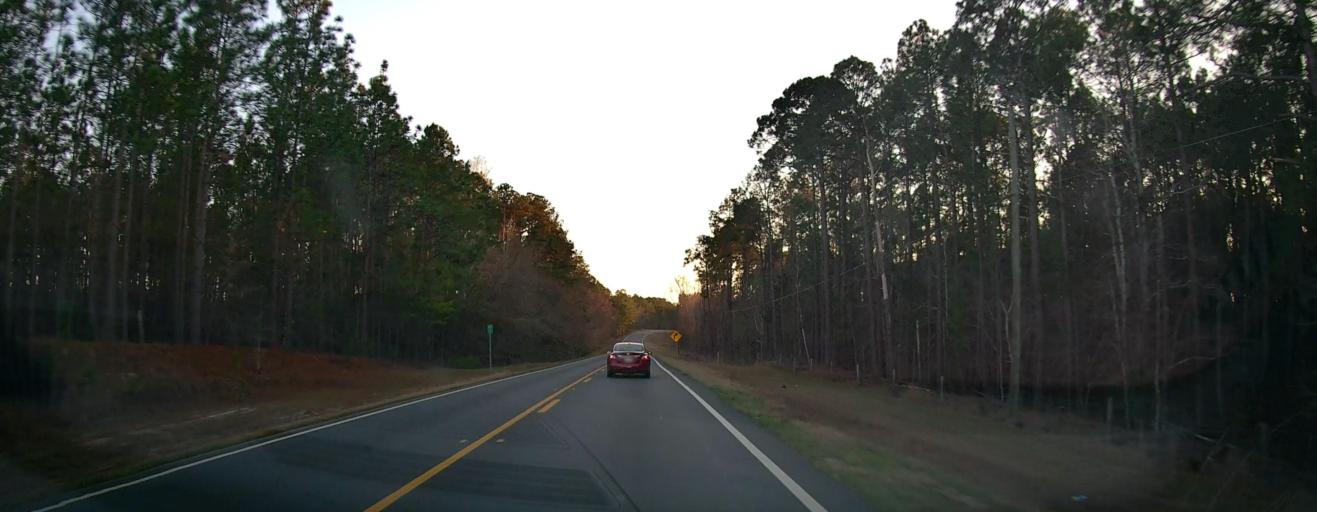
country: US
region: Georgia
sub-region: Dodge County
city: Chester
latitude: 32.3244
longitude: -83.0509
